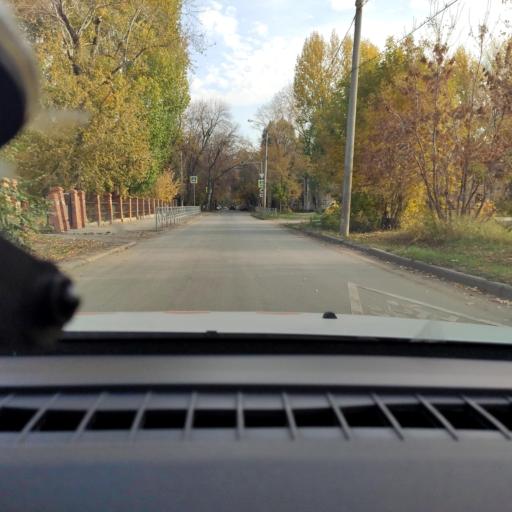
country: RU
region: Samara
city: Samara
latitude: 53.1192
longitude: 50.0777
